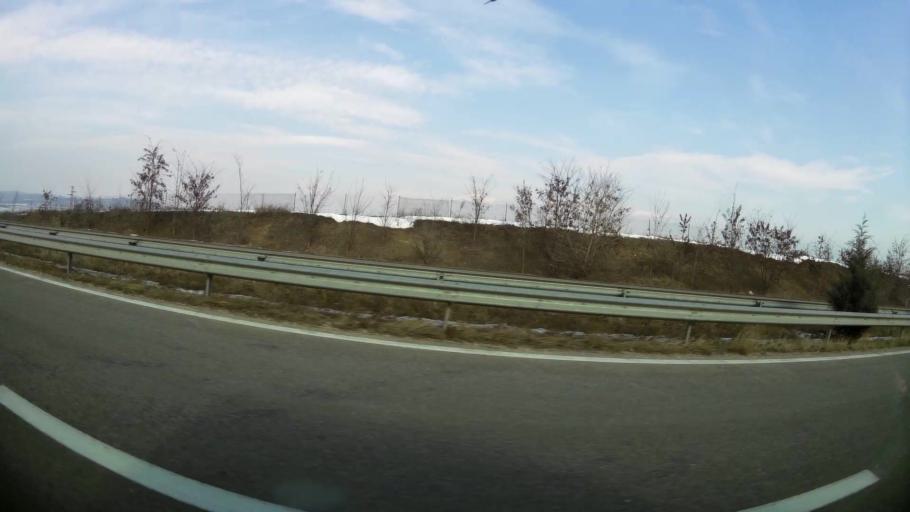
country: MK
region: Suto Orizari
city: Suto Orizare
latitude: 42.0495
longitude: 21.4328
